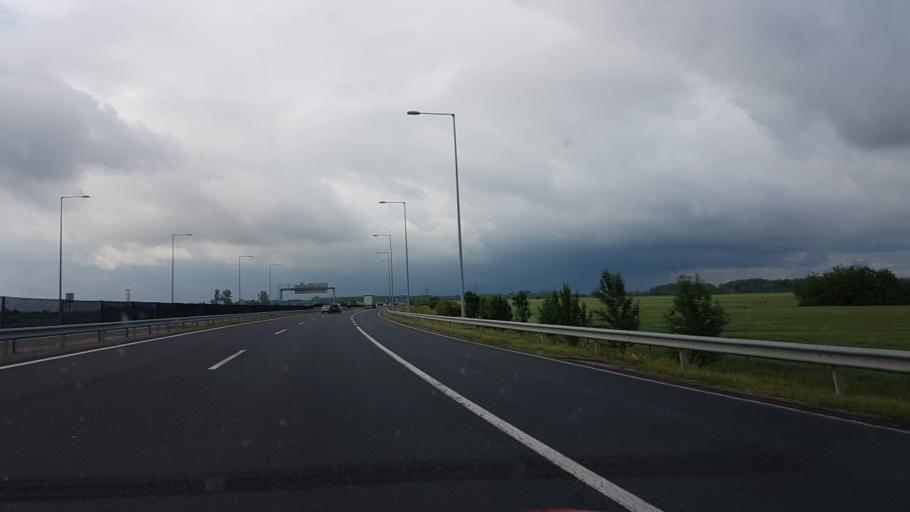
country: HU
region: Borsod-Abauj-Zemplen
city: Alsozsolca
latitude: 48.0636
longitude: 20.8452
